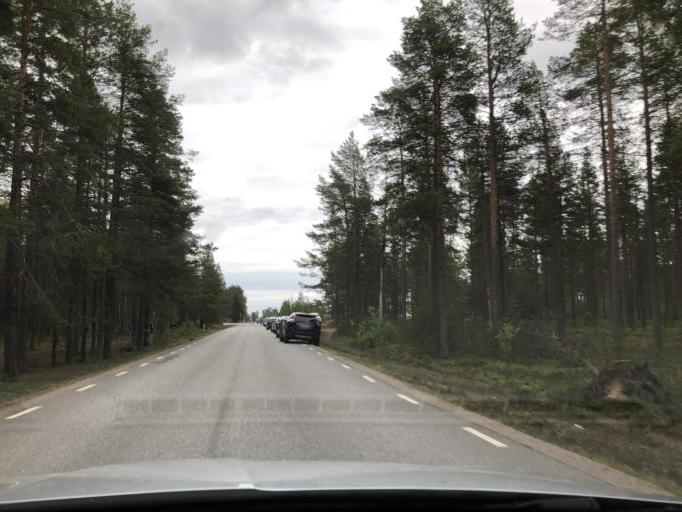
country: SE
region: Norrbotten
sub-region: Pitea Kommun
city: Pitea
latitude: 65.2378
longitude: 21.5217
